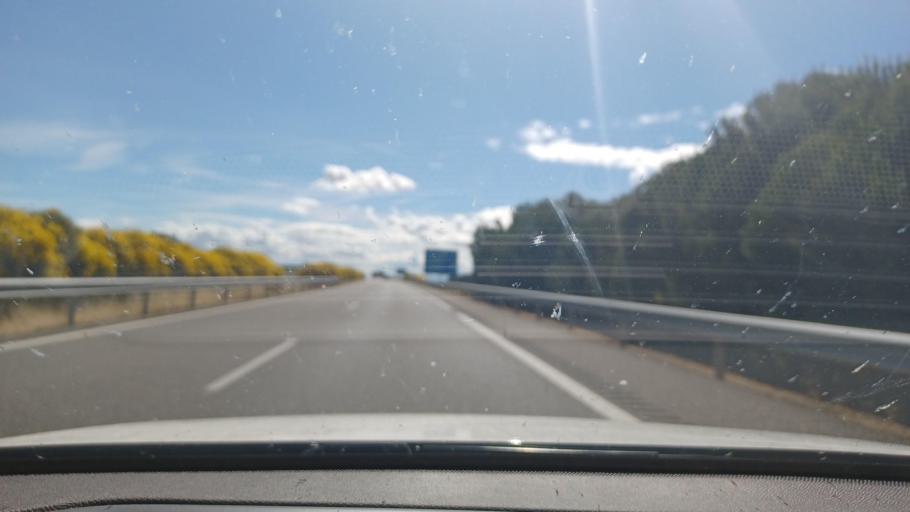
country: ES
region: Castille and Leon
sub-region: Provincia de Leon
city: Villanueva de las Manzanas
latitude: 42.4569
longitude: -5.4814
